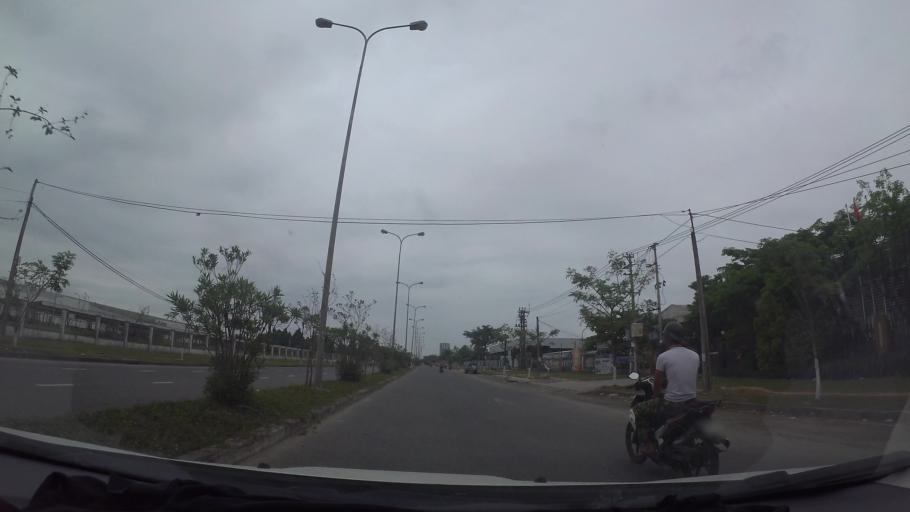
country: VN
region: Da Nang
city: Lien Chieu
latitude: 16.0751
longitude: 108.1380
